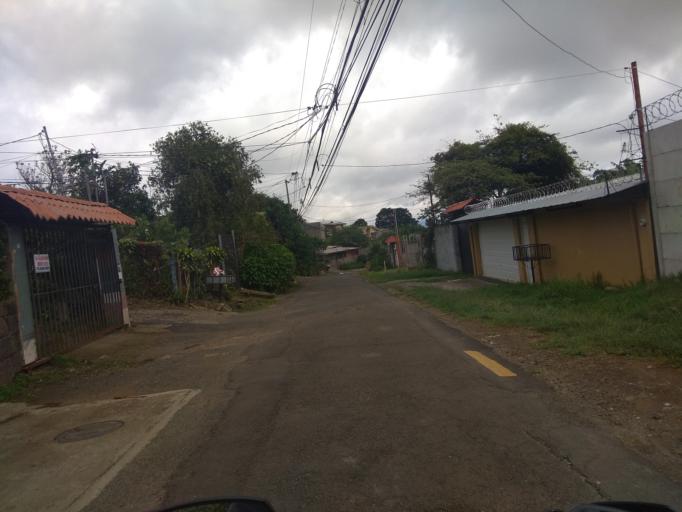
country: CR
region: Heredia
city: San Josecito
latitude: 10.0304
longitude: -84.0972
